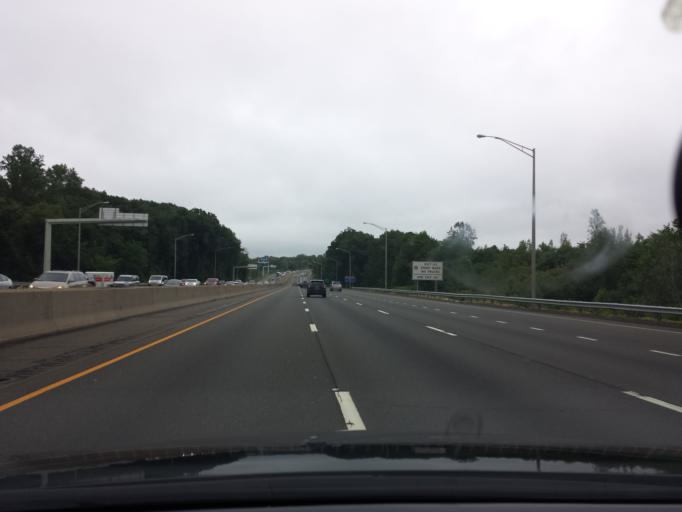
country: US
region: Connecticut
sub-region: New Haven County
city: Woodmont
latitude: 41.2560
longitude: -72.9958
